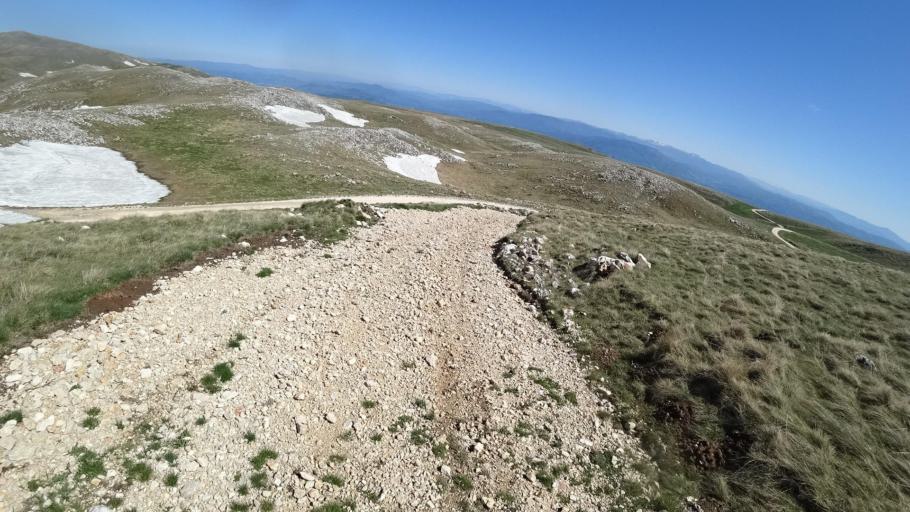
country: BA
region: Federation of Bosnia and Herzegovina
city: Travnik
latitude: 44.2855
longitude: 17.6374
